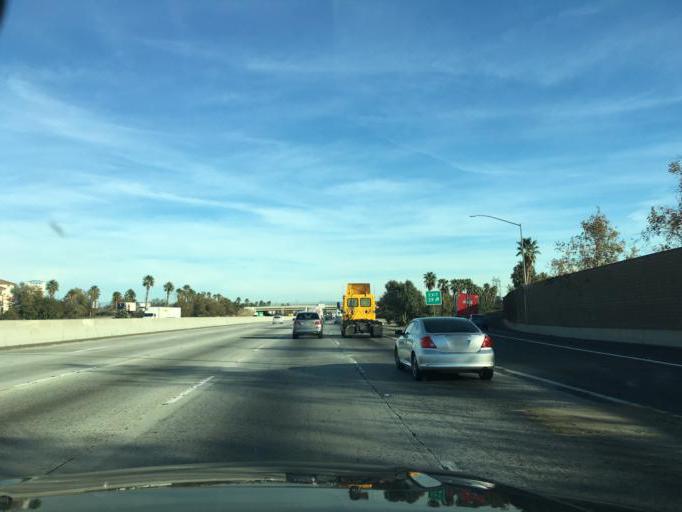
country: US
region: California
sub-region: Riverside County
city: Mira Loma
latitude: 34.0297
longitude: -117.5796
